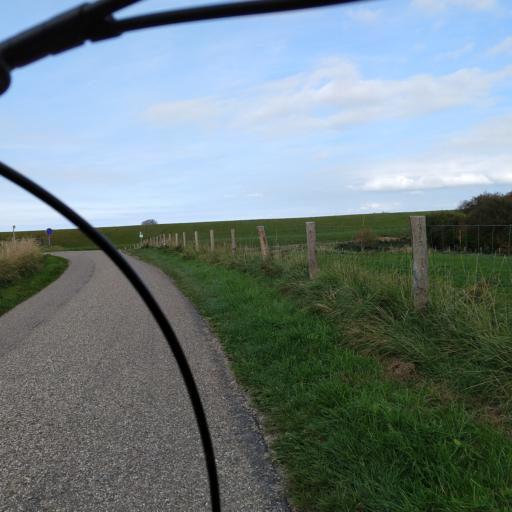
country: NL
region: South Holland
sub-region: Gemeente Goeree-Overflakkee
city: Ouddorp
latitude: 51.7319
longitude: 3.9443
